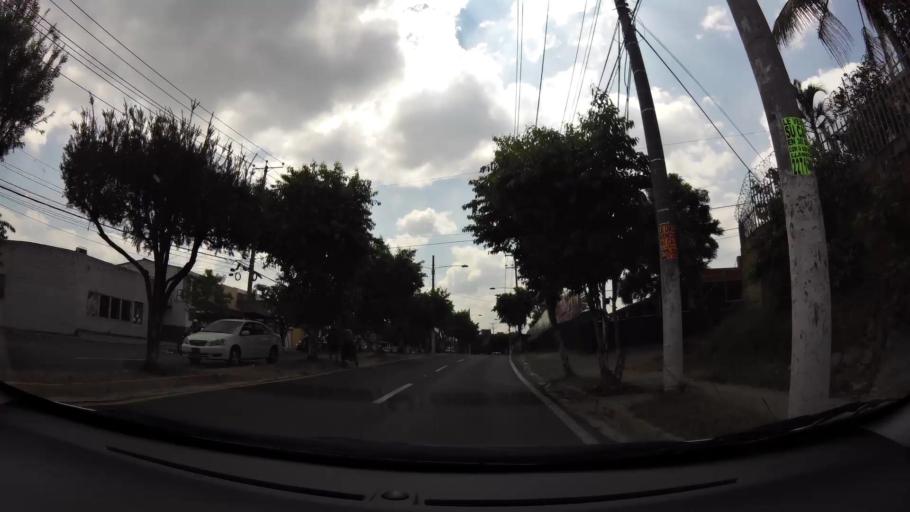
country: SV
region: San Salvador
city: Mejicanos
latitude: 13.7128
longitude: -89.2312
